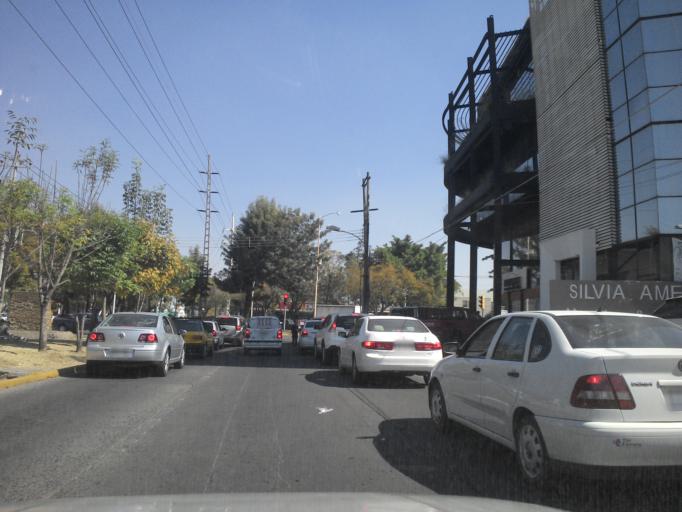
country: MX
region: Jalisco
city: Guadalajara
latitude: 20.6872
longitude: -103.3797
